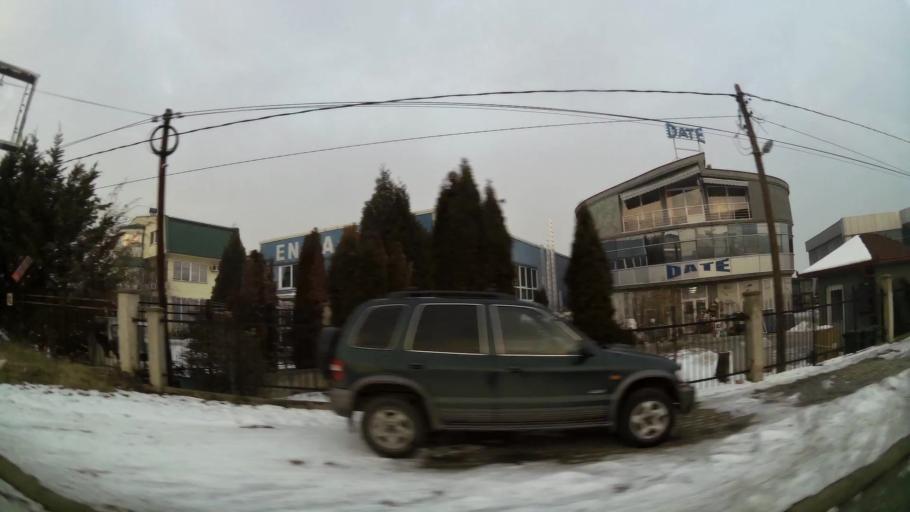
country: MK
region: Suto Orizari
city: Suto Orizare
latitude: 42.0373
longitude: 21.3989
